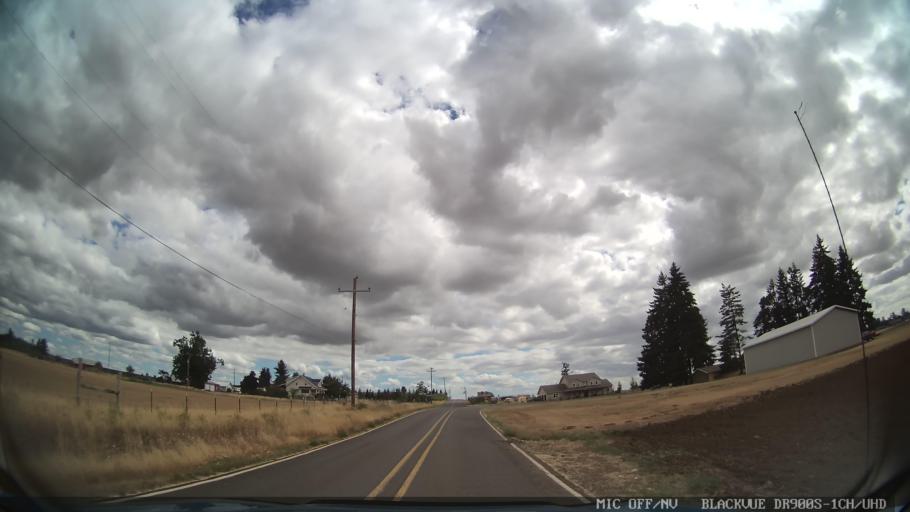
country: US
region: Oregon
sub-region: Marion County
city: Sublimity
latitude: 44.8415
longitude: -122.7741
